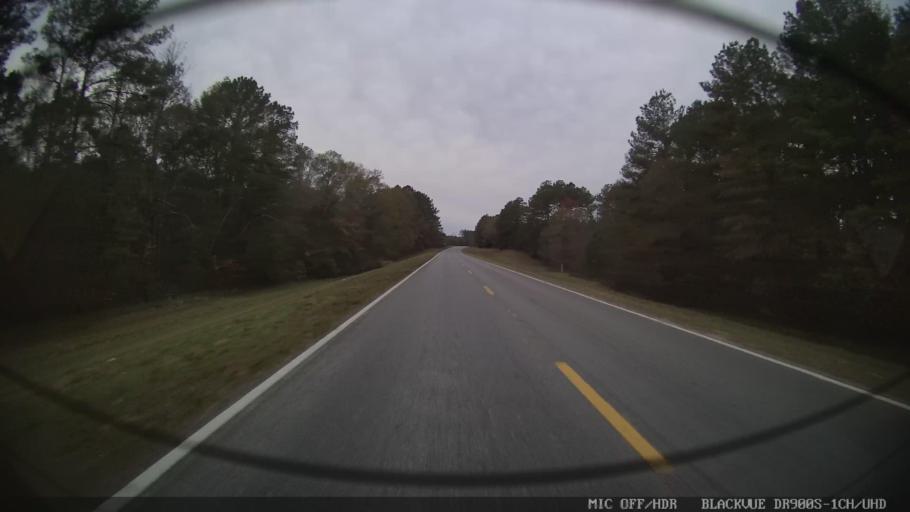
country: US
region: Mississippi
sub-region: Clarke County
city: Quitman
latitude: 32.0258
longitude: -88.8399
